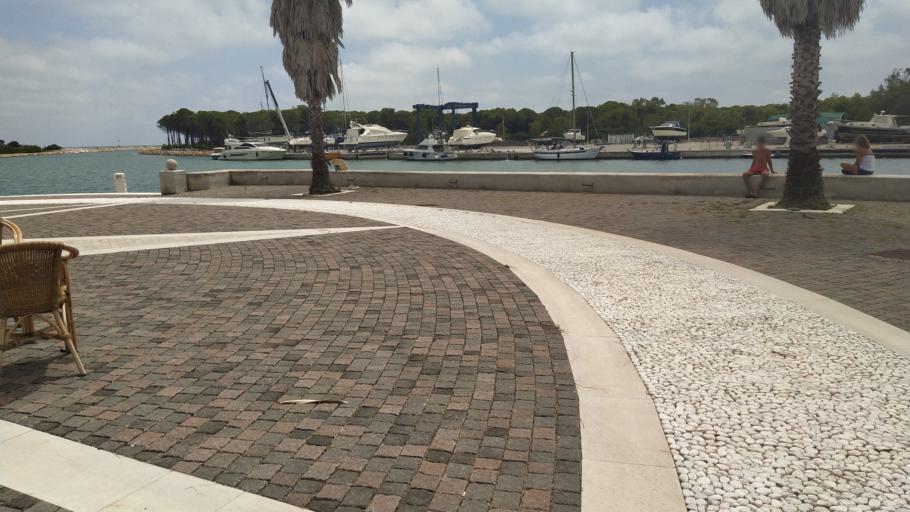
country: IT
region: Apulia
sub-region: Provincia di Taranto
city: Marina di Ginosa
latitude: 40.3388
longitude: 16.8125
